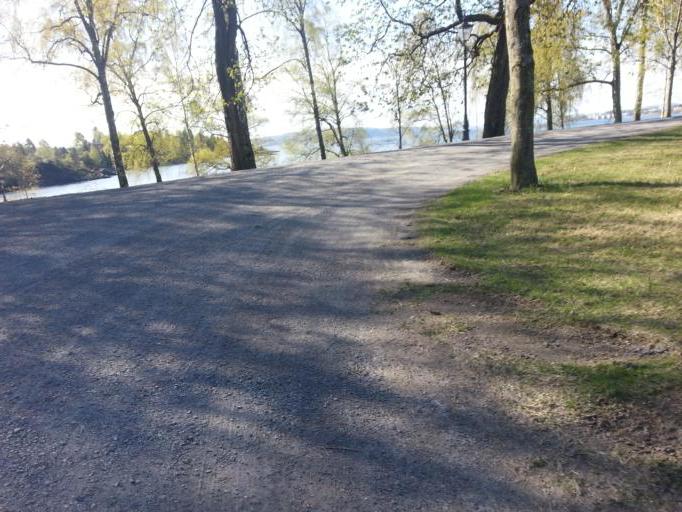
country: NO
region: Akershus
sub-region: Baerum
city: Lysaker
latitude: 59.9148
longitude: 10.6560
